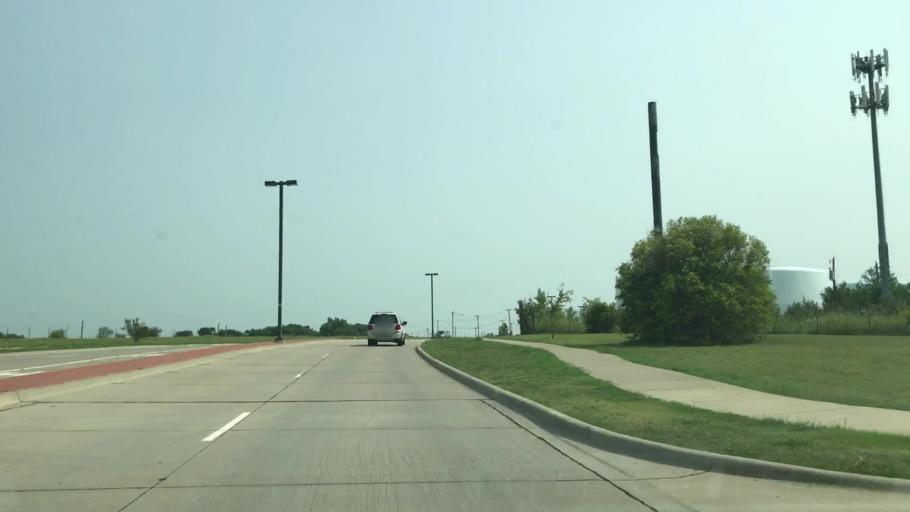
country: US
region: Texas
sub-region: Dallas County
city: Sachse
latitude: 32.9450
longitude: -96.5699
